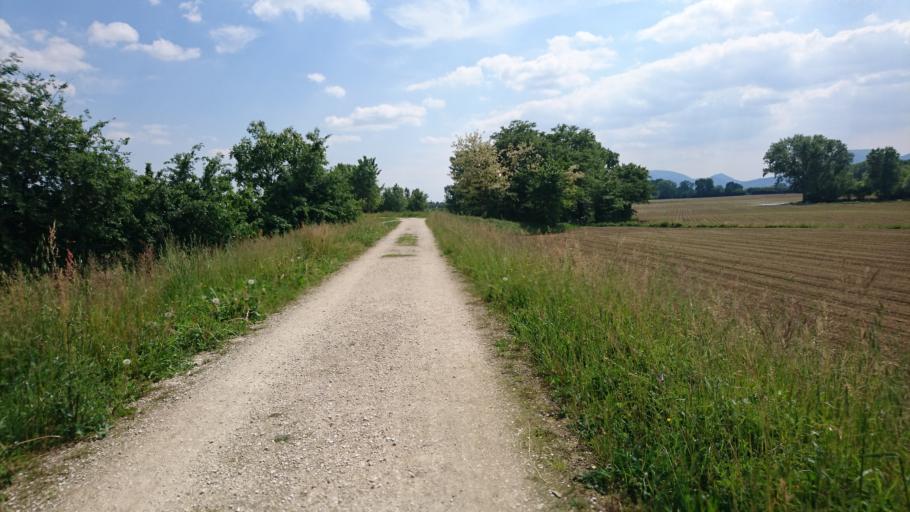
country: IT
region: Veneto
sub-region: Provincia di Padova
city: Veggiano
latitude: 45.4317
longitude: 11.7272
